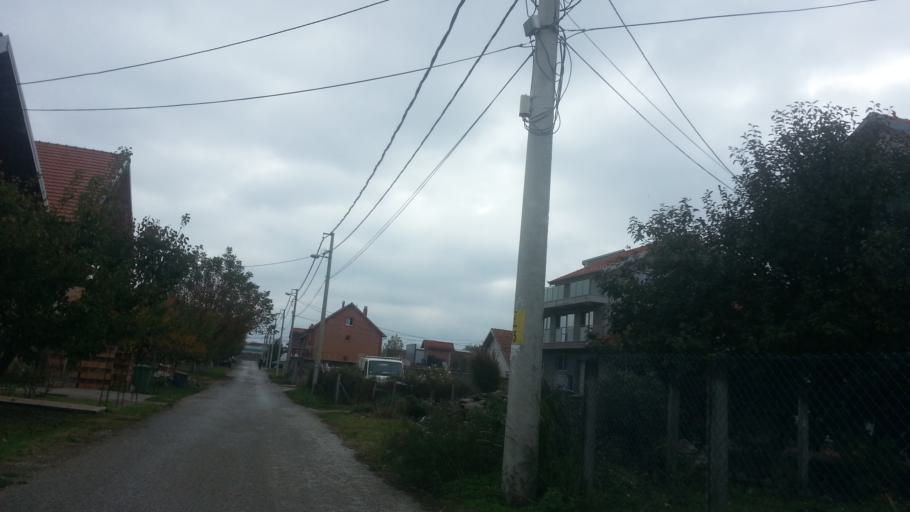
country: RS
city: Novi Banovci
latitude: 44.8995
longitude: 20.2985
